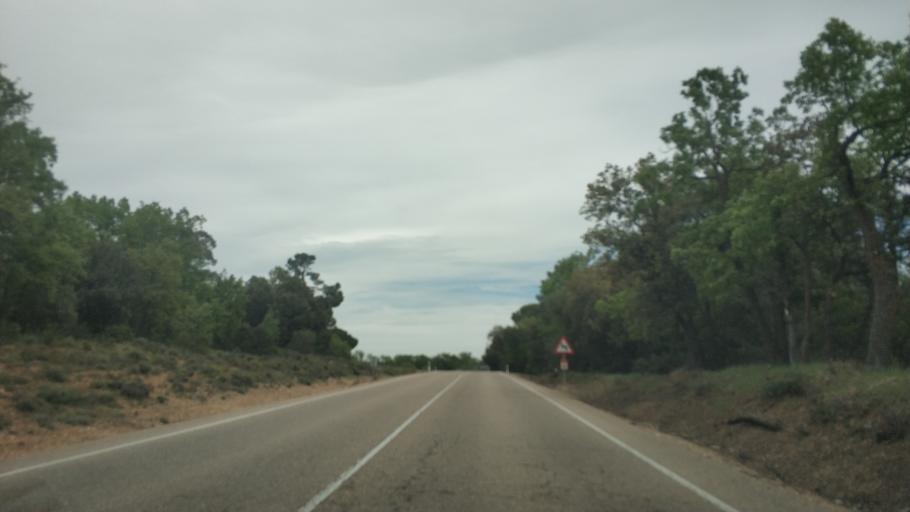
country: ES
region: Castille and Leon
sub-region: Provincia de Soria
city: Bayubas de Abajo
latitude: 41.5047
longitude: -2.8987
